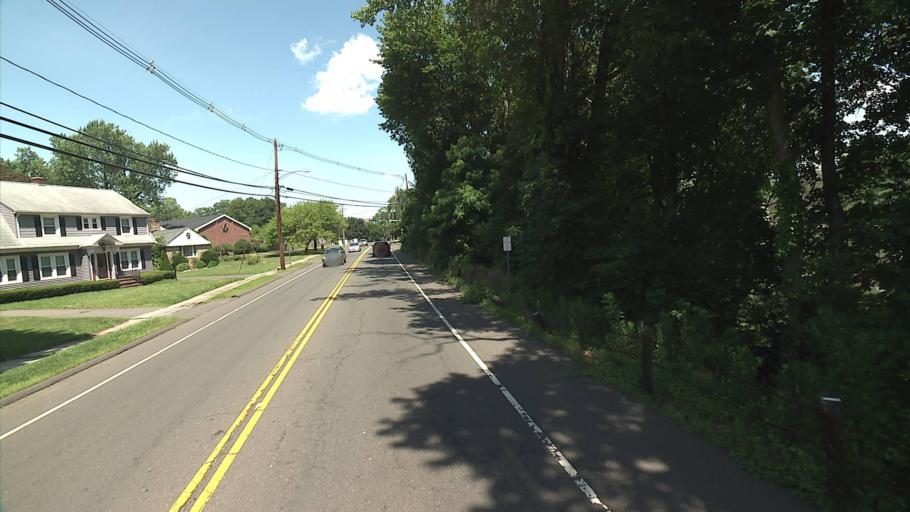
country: US
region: Connecticut
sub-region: Hartford County
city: New Britain
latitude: 41.6522
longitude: -72.7951
